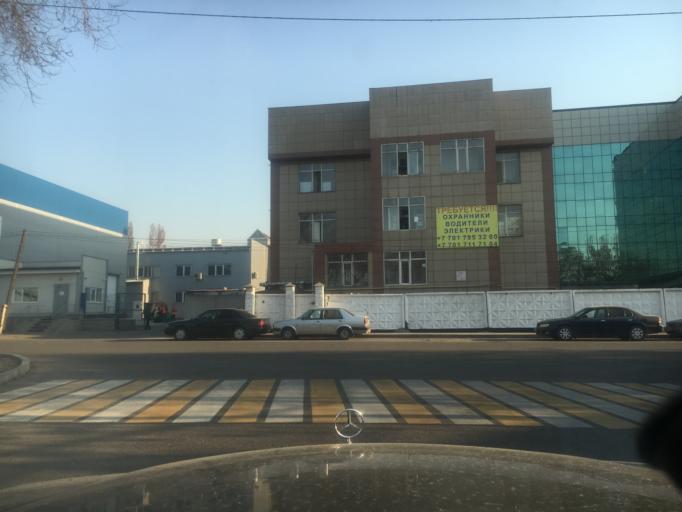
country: KZ
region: Almaty Qalasy
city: Almaty
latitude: 43.2766
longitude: 76.9416
